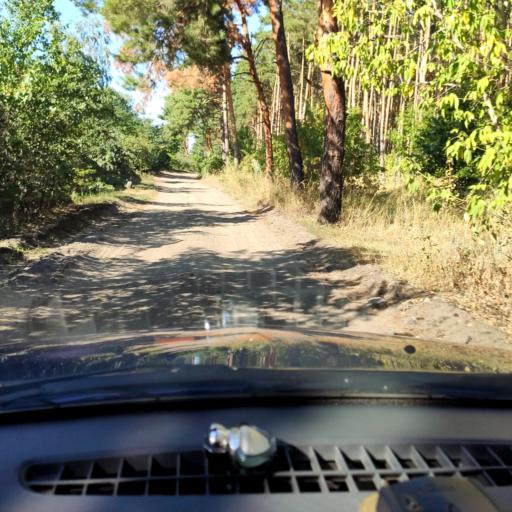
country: RU
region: Voronezj
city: Shilovo
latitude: 51.5340
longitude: 39.1584
